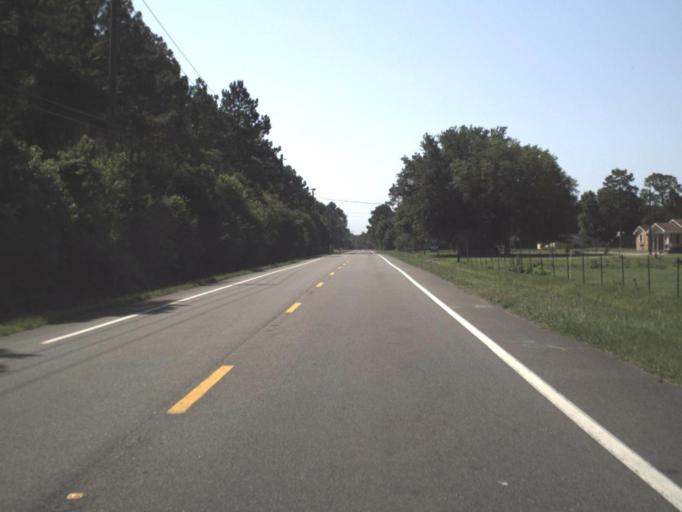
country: US
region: Florida
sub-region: Nassau County
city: Nassau Village-Ratliff
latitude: 30.4824
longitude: -81.7188
